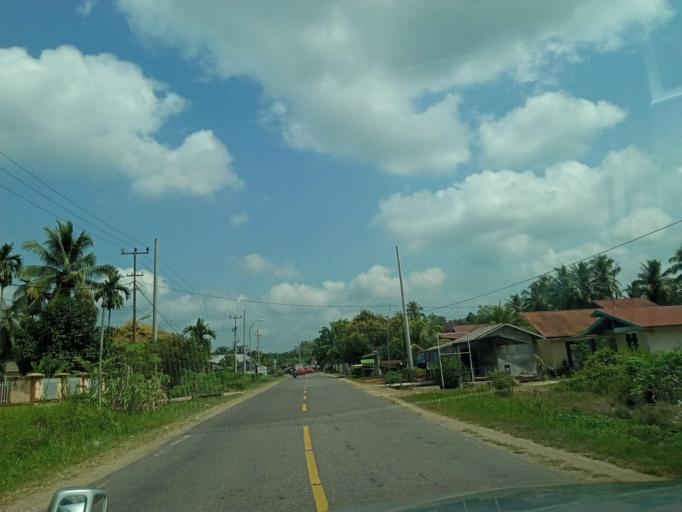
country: ID
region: Jambi
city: Muara Tembesi
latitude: -1.7202
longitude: 103.1266
